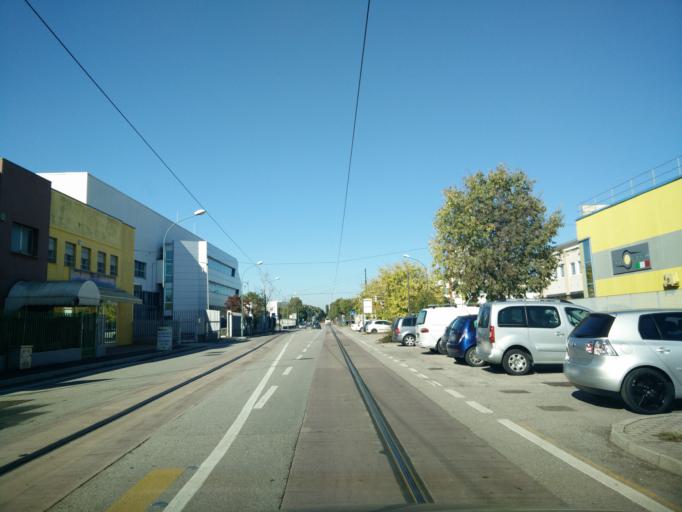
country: IT
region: Veneto
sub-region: Provincia di Venezia
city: Mestre
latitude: 45.4626
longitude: 12.2167
